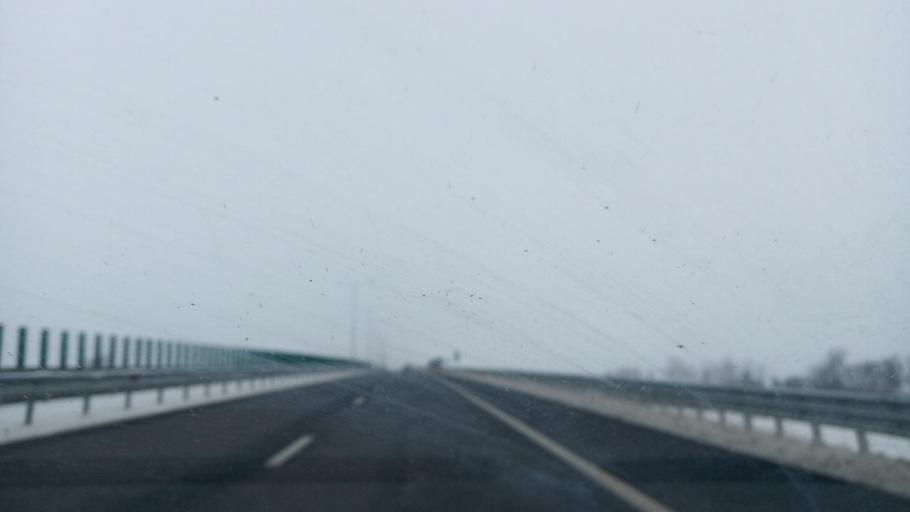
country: RO
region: Bacau
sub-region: Comuna Letea Veche
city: Holt
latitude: 46.5992
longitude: 26.9605
